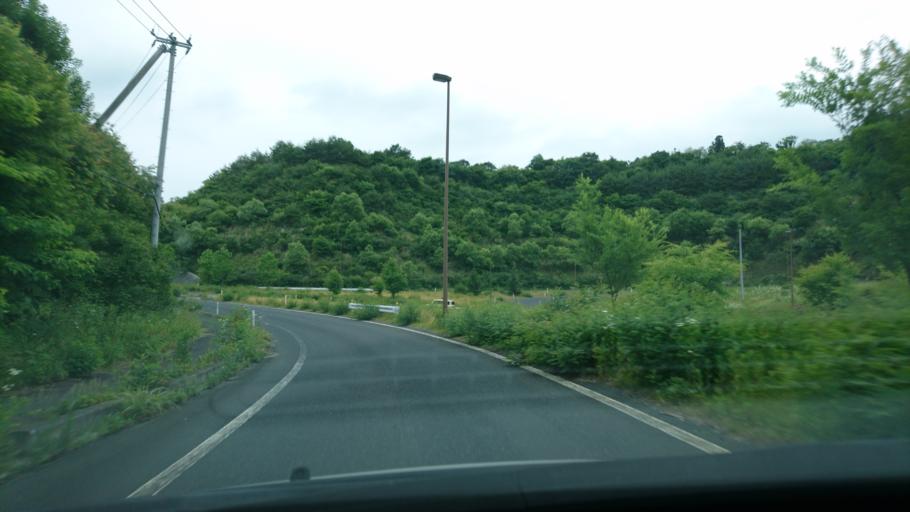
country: JP
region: Iwate
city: Ichinoseki
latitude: 38.9313
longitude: 141.1672
